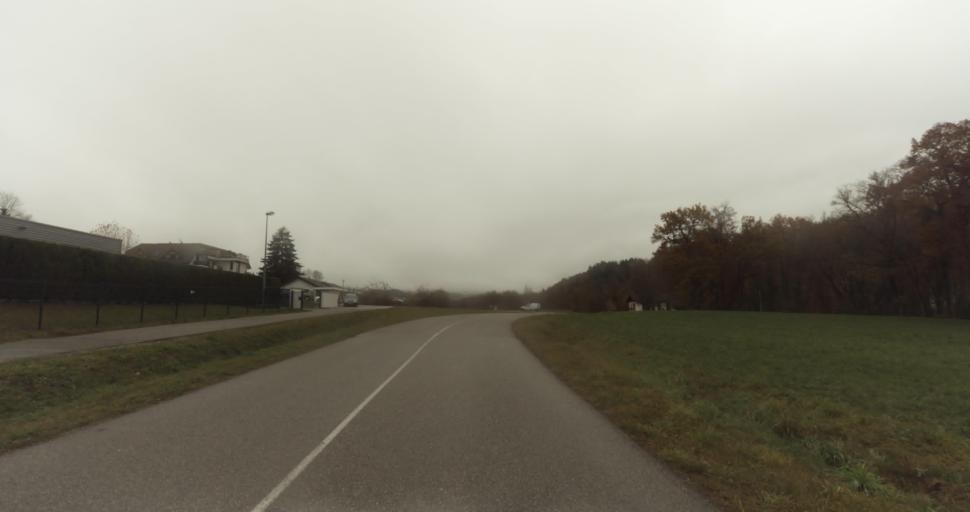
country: FR
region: Rhone-Alpes
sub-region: Departement de la Haute-Savoie
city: Saint-Martin-Bellevue
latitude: 45.9618
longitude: 6.1666
